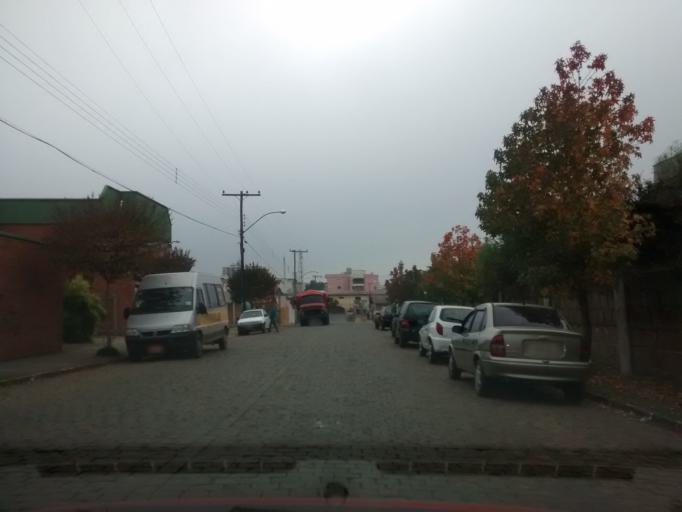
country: BR
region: Rio Grande do Sul
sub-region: Vacaria
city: Vacaria
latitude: -28.5078
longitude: -50.9434
